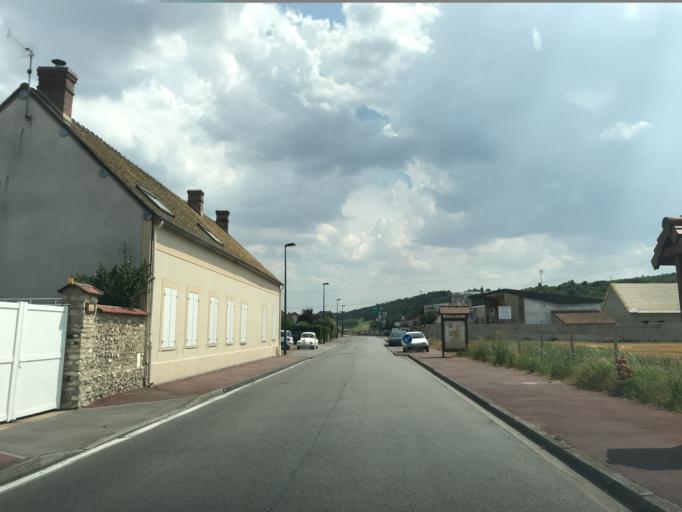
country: FR
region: Haute-Normandie
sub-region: Departement de l'Eure
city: Garennes-sur-Eure
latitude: 48.9085
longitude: 1.4419
